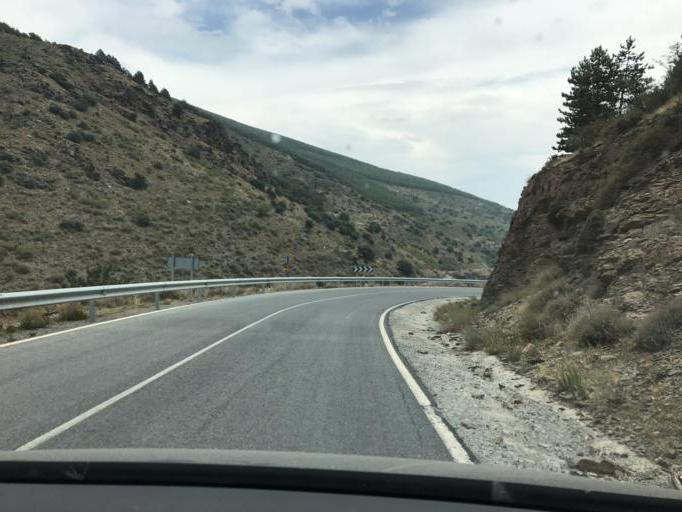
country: ES
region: Andalusia
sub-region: Provincia de Almeria
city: Bayarcal
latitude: 37.0767
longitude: -3.0216
